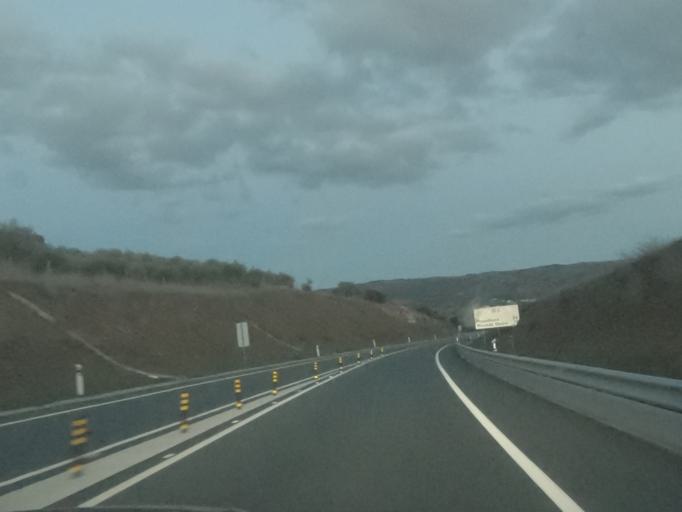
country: PT
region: Braganca
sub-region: Alfandega da Fe
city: Alfandega da Fe
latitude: 41.3243
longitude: -6.9359
